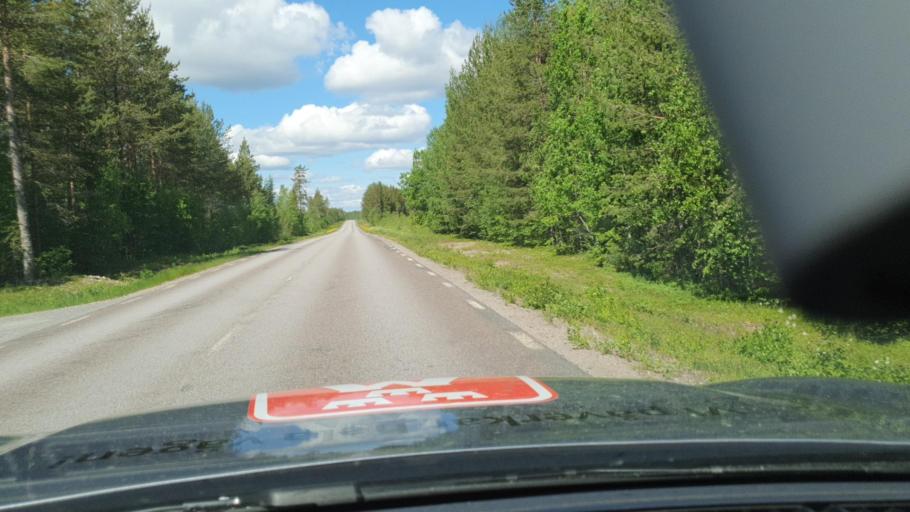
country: SE
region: Norrbotten
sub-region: Pitea Kommun
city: Rosvik
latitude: 65.5199
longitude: 21.6888
